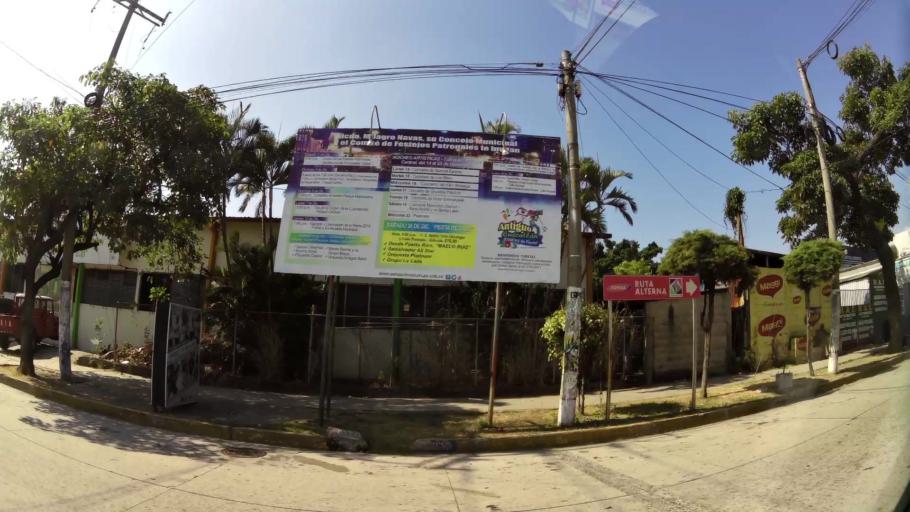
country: SV
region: La Libertad
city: Antiguo Cuscatlan
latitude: 13.6750
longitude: -89.2438
